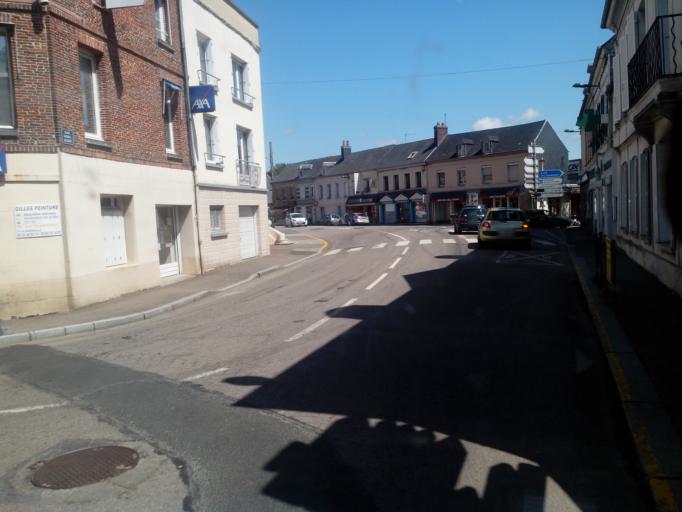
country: FR
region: Haute-Normandie
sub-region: Departement de la Seine-Maritime
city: Gonneville-la-Mallet
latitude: 49.6435
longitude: 0.2653
